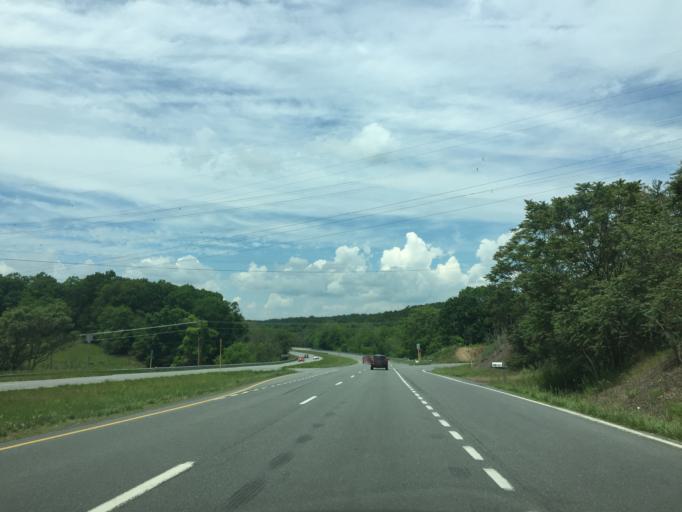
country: US
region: Virginia
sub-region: Frederick County
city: Shawnee Land
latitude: 39.2815
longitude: -78.2568
